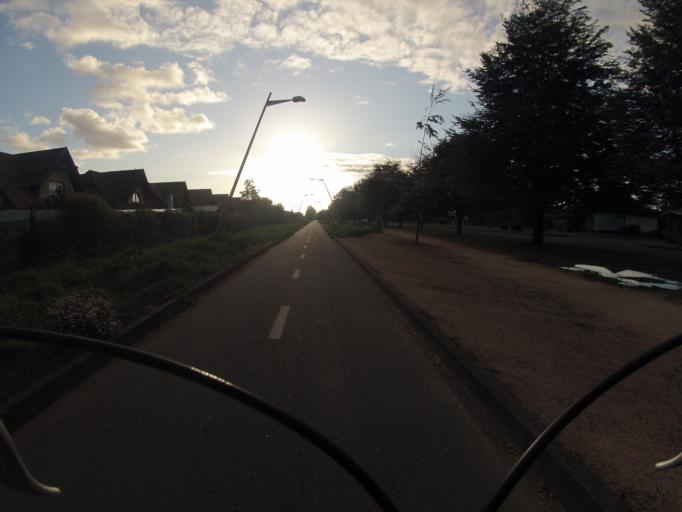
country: CL
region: Araucania
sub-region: Provincia de Cautin
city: Temuco
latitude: -38.7467
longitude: -72.6251
